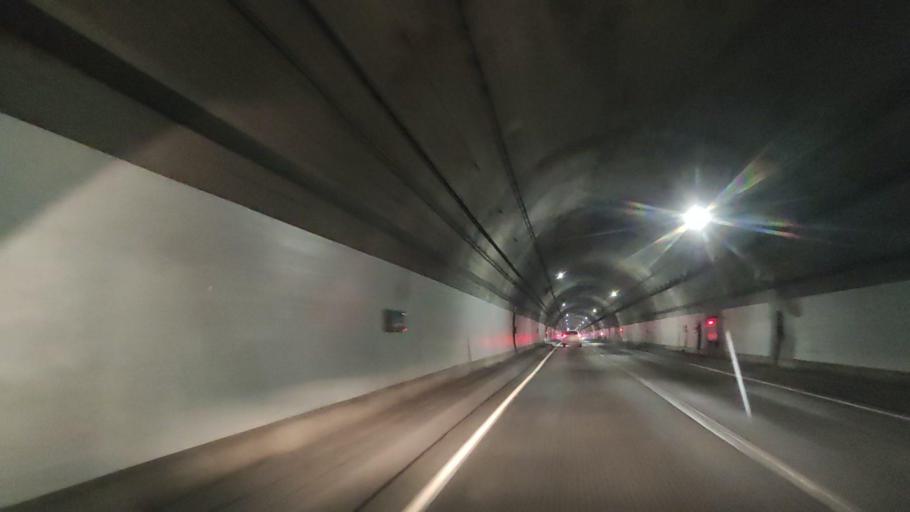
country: JP
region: Hokkaido
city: Rumoi
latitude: 43.7083
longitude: 141.3335
